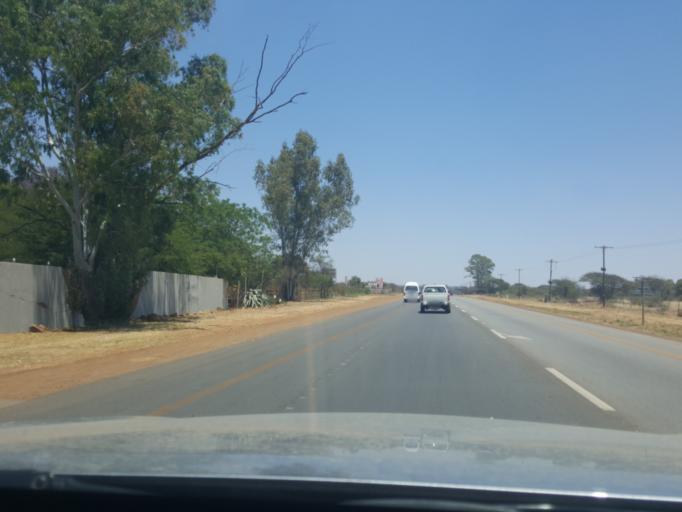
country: ZA
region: North-West
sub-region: Ngaka Modiri Molema District Municipality
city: Zeerust
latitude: -25.5542
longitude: 26.0699
